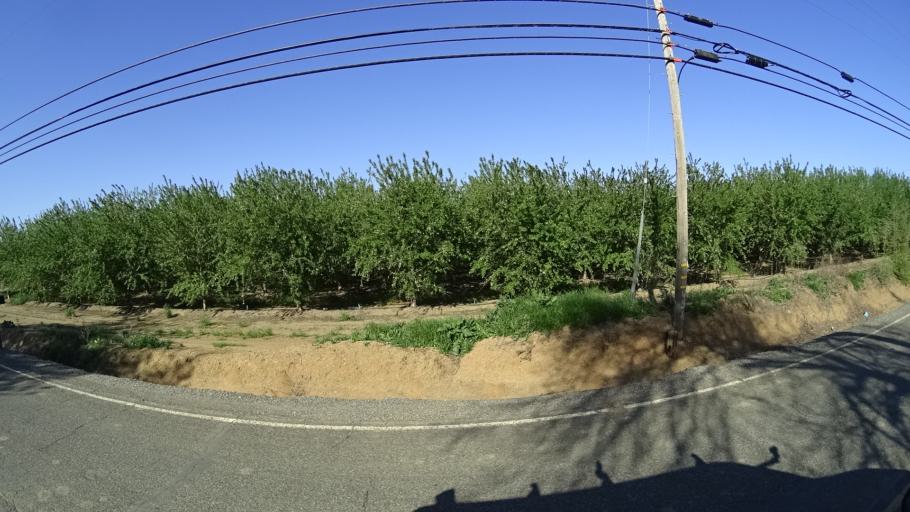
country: US
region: California
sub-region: Glenn County
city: Orland
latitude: 39.7818
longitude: -122.1041
